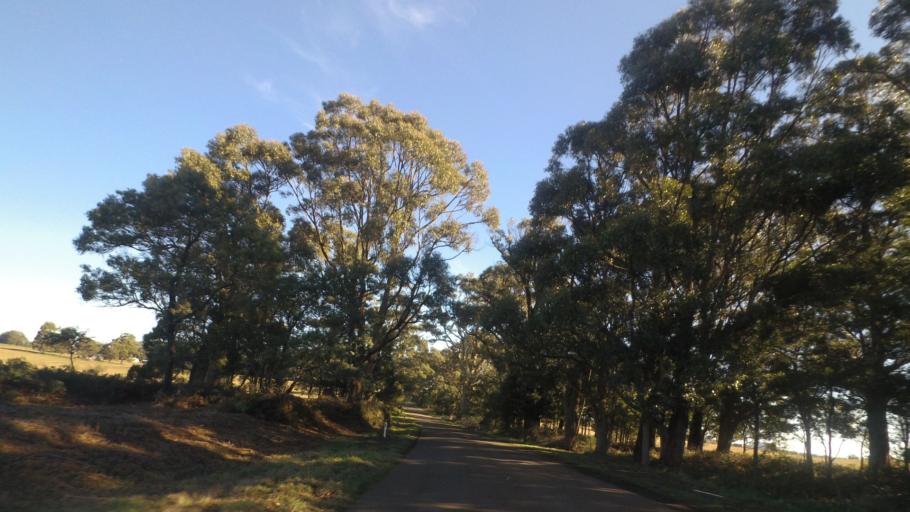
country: AU
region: Victoria
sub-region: Mount Alexander
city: Castlemaine
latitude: -37.3480
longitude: 144.2943
